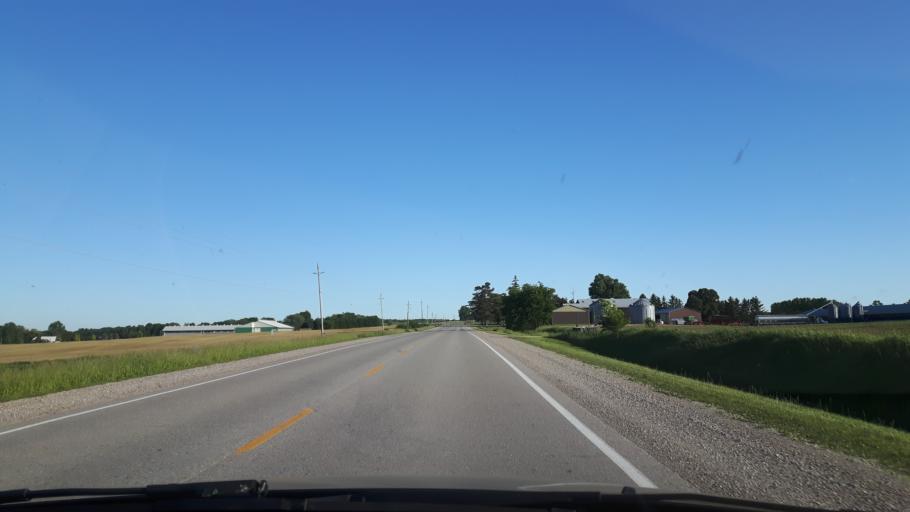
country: CA
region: Ontario
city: Bluewater
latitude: 43.5952
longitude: -81.6021
